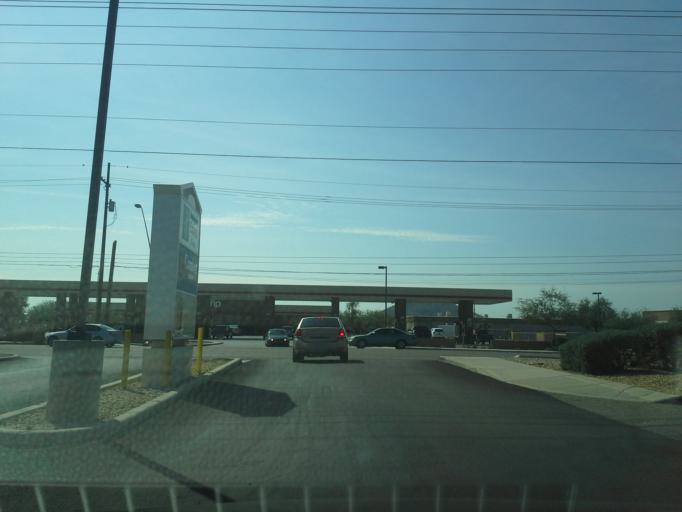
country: US
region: Arizona
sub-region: Pima County
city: Flowing Wells
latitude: 32.2509
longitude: -110.9984
